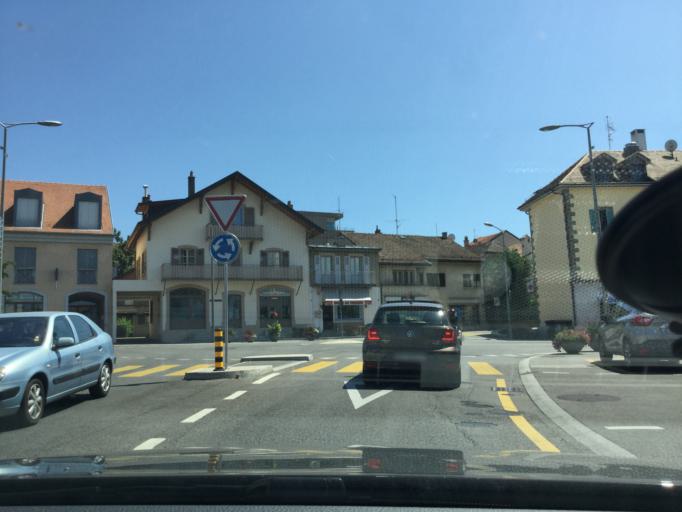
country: CH
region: Geneva
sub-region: Geneva
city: Vandoeuvres
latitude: 46.2400
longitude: 6.1980
